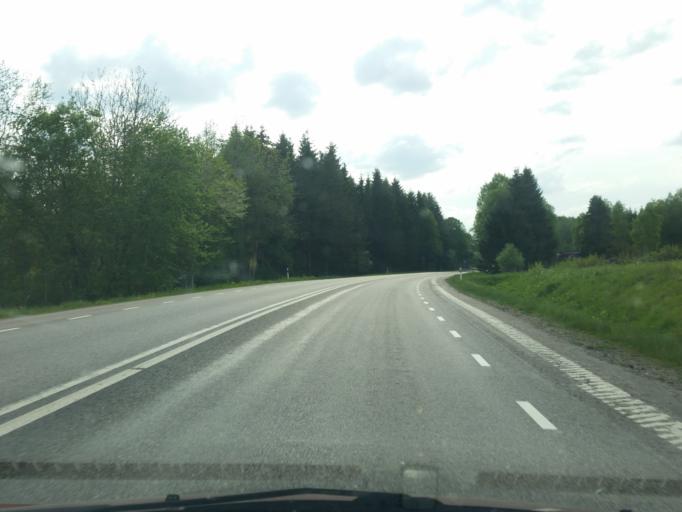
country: SE
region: Vaestra Goetaland
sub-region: Ulricehamns Kommun
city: Ulricehamn
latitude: 57.8076
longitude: 13.2476
